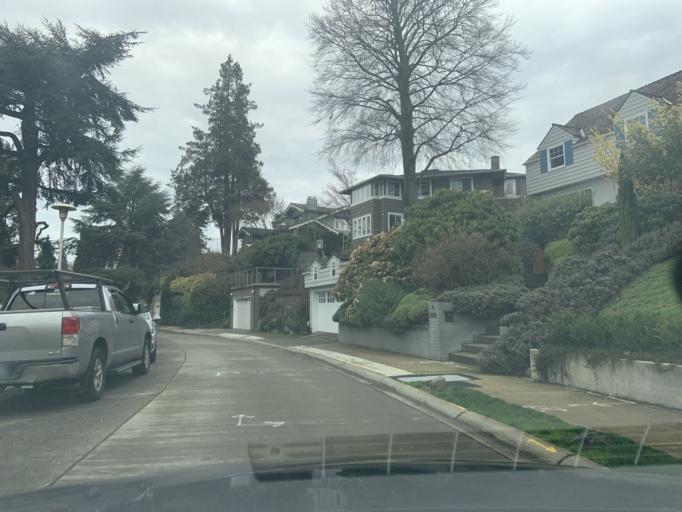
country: US
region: Washington
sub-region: King County
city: Medina
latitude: 47.6495
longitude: -122.2772
